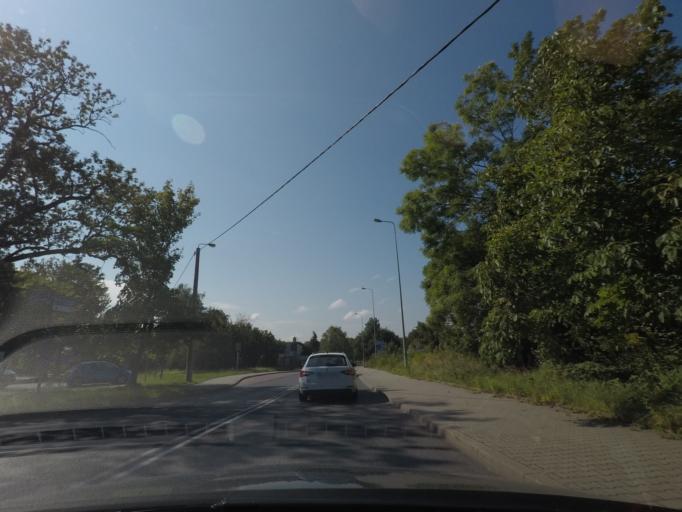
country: PL
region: Lesser Poland Voivodeship
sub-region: Powiat chrzanowski
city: Chrzanow
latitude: 50.1476
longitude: 19.4003
